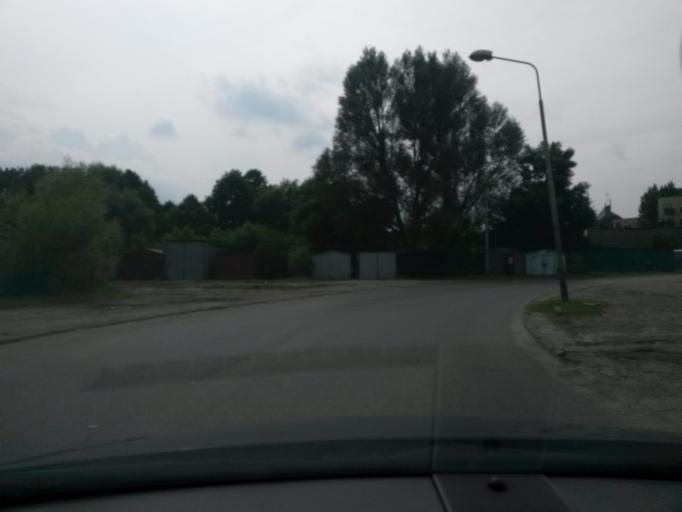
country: PL
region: Silesian Voivodeship
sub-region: Czestochowa
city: Czestochowa
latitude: 50.7716
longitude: 19.1567
